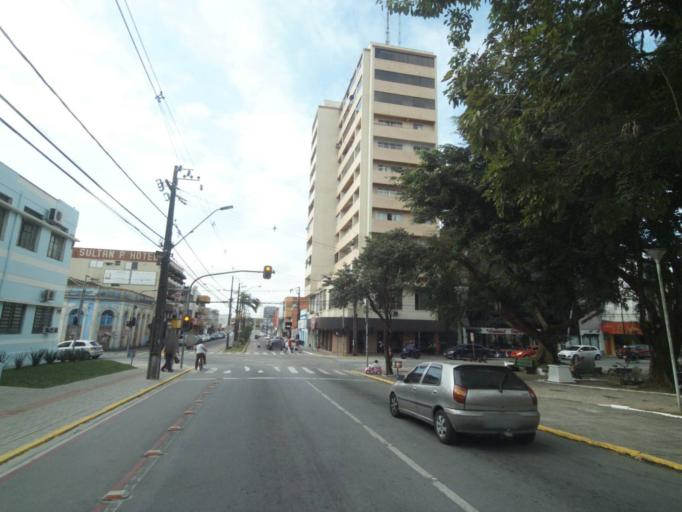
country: BR
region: Parana
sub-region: Paranagua
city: Paranagua
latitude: -25.5190
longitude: -48.5088
